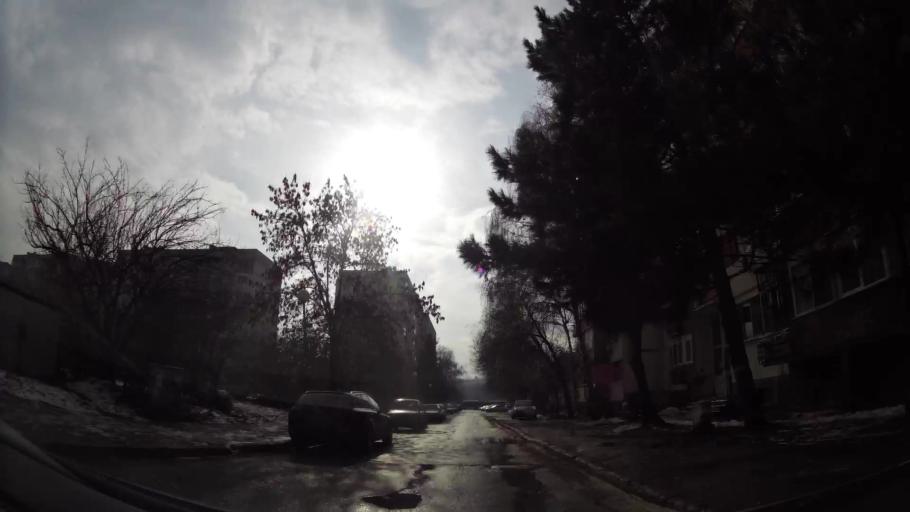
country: BG
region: Sofiya
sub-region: Obshtina Bozhurishte
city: Bozhurishte
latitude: 42.7101
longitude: 23.2483
